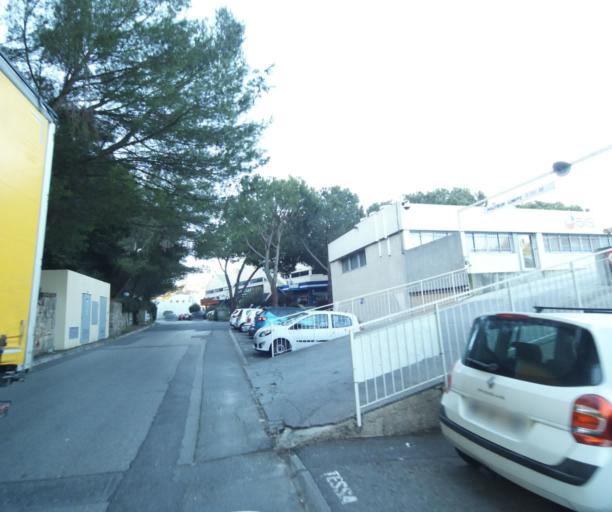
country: FR
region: Provence-Alpes-Cote d'Azur
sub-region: Departement des Alpes-Maritimes
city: Vallauris
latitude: 43.6024
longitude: 7.0625
